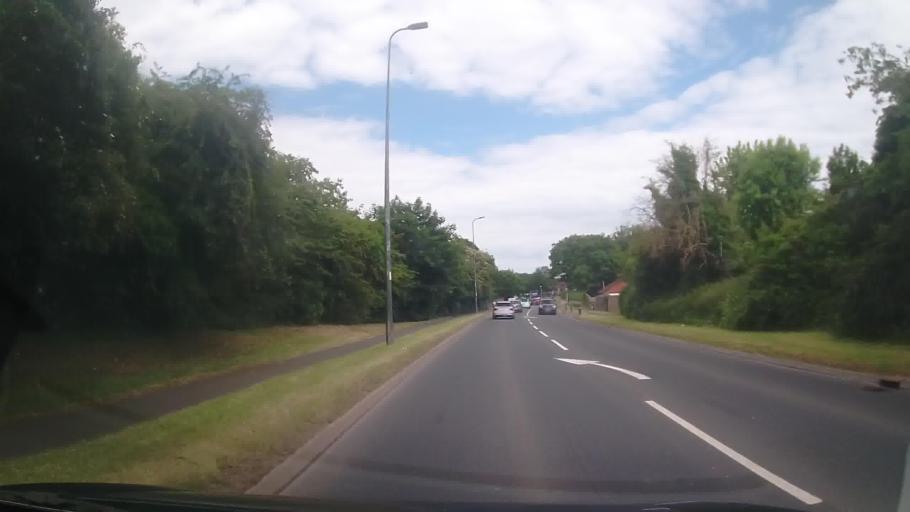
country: GB
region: England
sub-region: Herefordshire
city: Belmont
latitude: 52.0422
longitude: -2.7378
